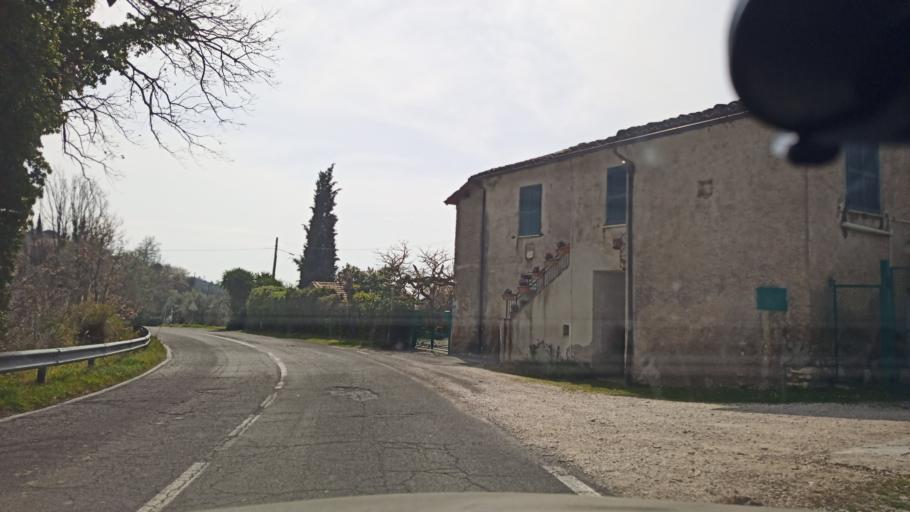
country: IT
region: Latium
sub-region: Provincia di Rieti
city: Torri in Sabina
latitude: 42.3490
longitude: 12.6496
